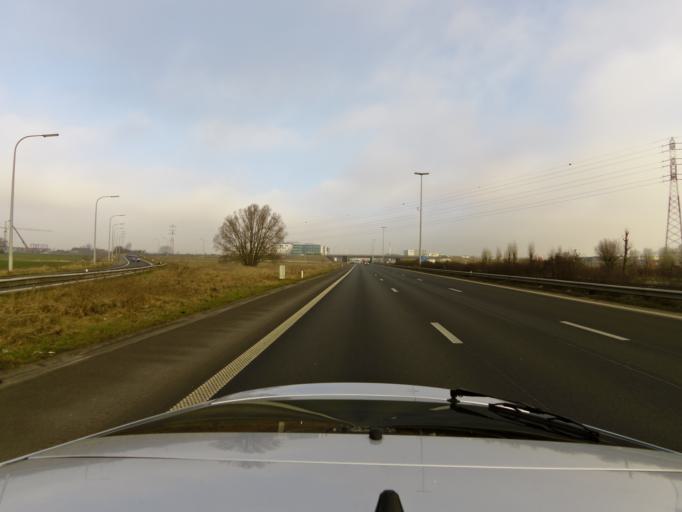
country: BE
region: Flanders
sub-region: Provincie West-Vlaanderen
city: Izegem
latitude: 50.9159
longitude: 3.1774
